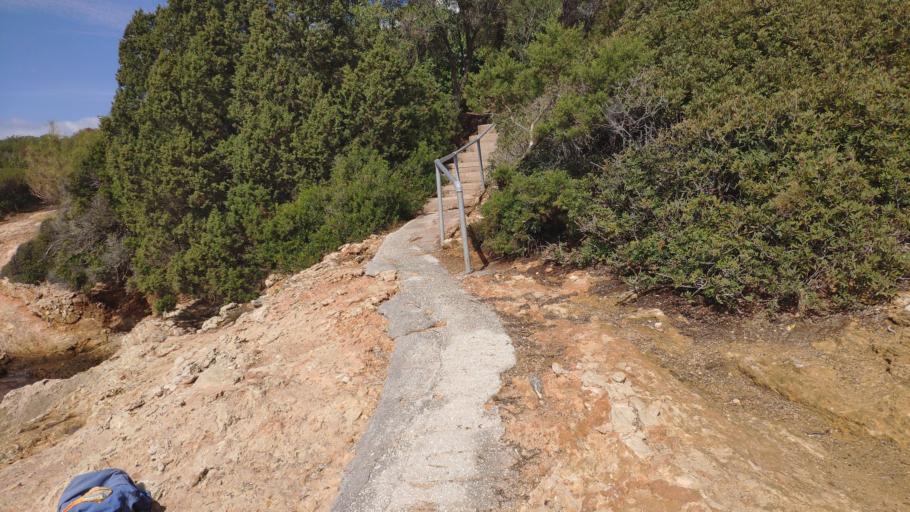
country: GR
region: Attica
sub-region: Nomarchia Anatolikis Attikis
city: Limin Mesoyaias
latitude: 37.8913
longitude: 24.0296
